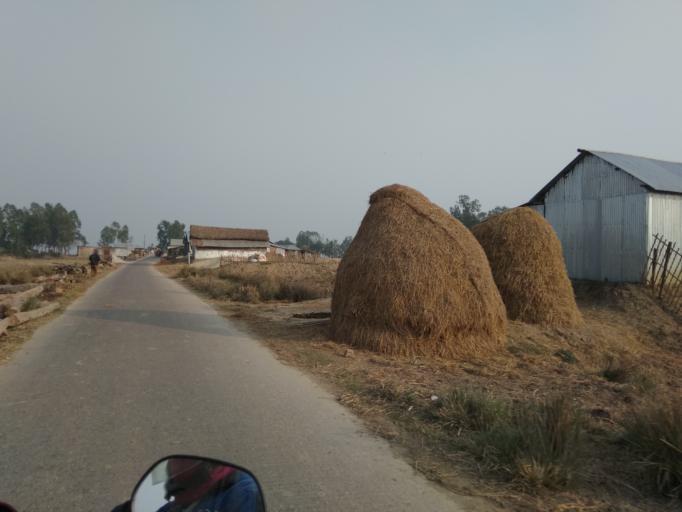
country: BD
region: Rajshahi
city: Ishurdi
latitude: 24.4935
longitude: 89.1987
